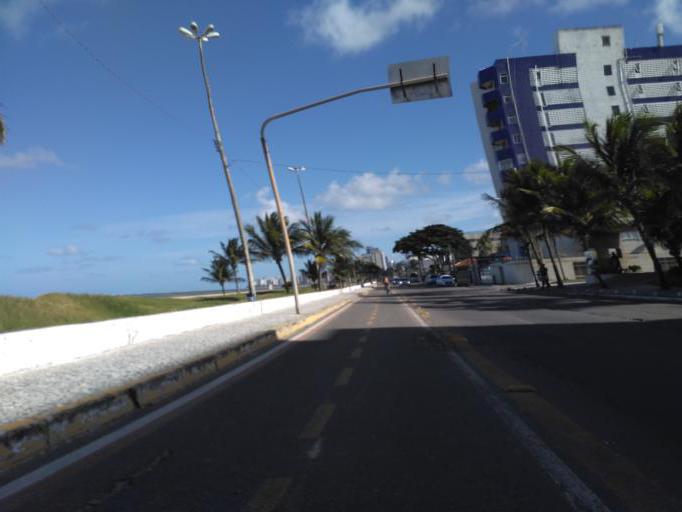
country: BR
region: Pernambuco
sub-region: Jaboatao Dos Guararapes
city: Jaboatao
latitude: -8.1619
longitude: -34.9121
